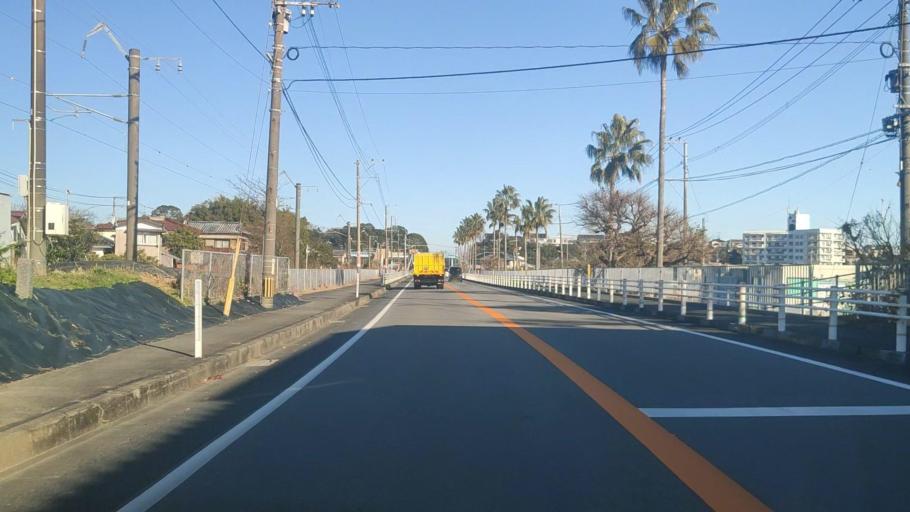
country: JP
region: Miyazaki
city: Nobeoka
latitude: 32.5142
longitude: 131.6824
